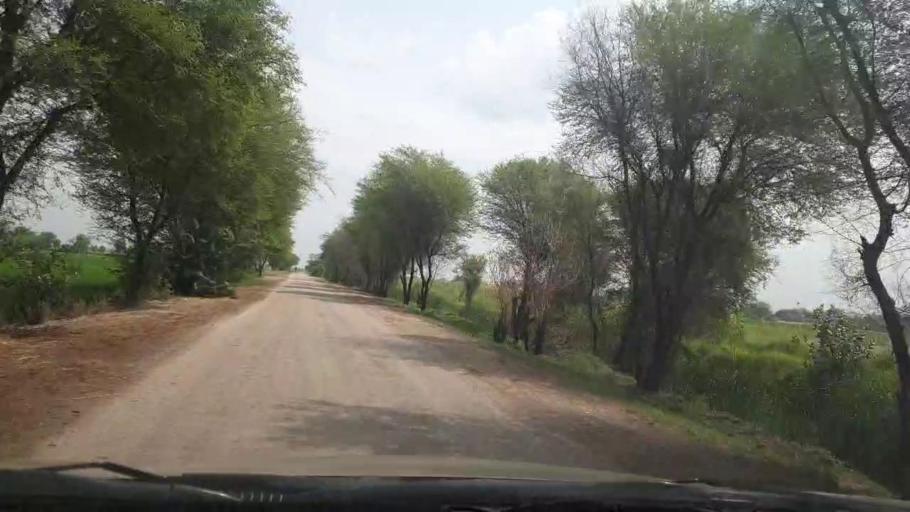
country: PK
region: Sindh
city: Miro Khan
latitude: 27.6927
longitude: 68.1968
